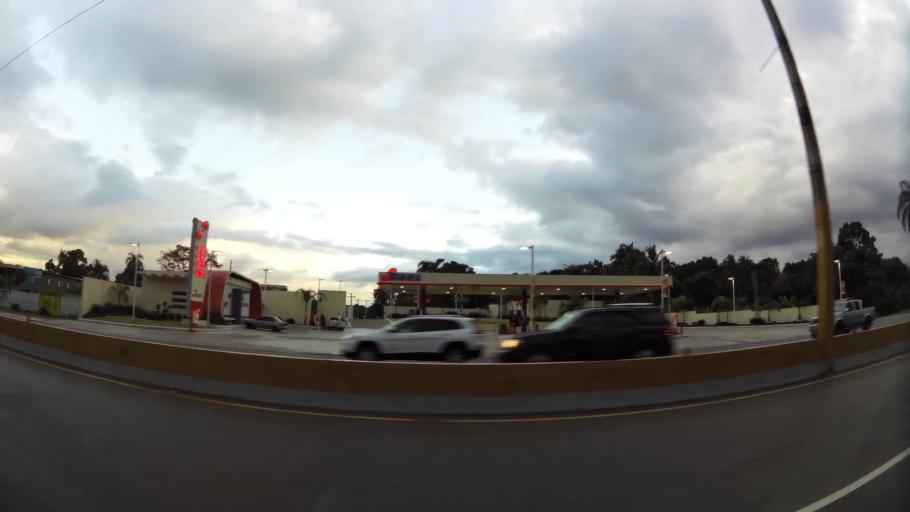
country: DO
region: Santo Domingo
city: Santo Domingo Oeste
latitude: 18.5662
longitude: -70.0834
